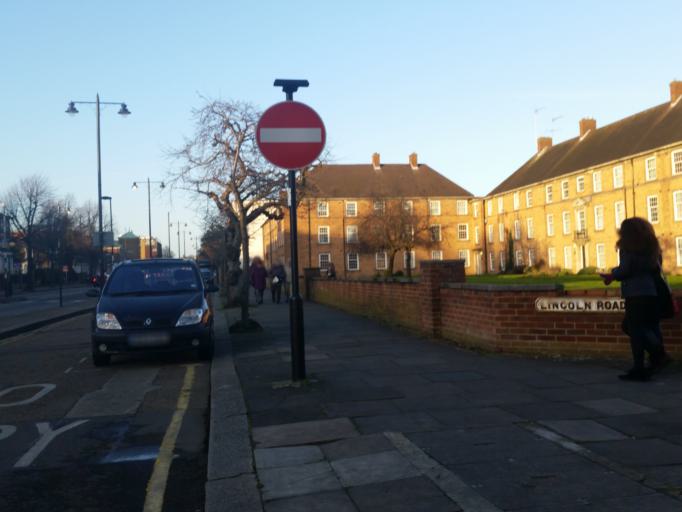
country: GB
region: England
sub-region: Greater London
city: Enfield
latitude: 51.6474
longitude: -0.0795
